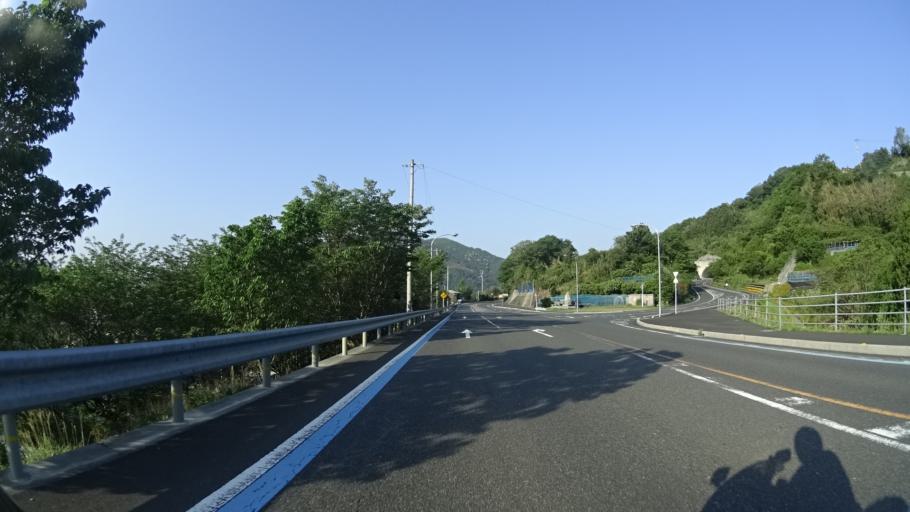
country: JP
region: Ehime
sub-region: Nishiuwa-gun
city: Ikata-cho
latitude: 33.4907
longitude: 132.3519
